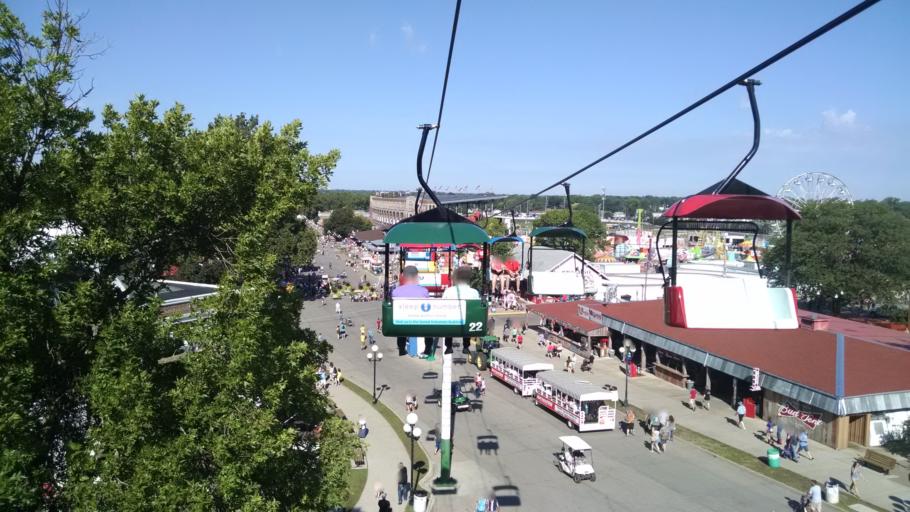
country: US
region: Iowa
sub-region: Polk County
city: Pleasant Hill
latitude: 41.5957
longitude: -93.5502
